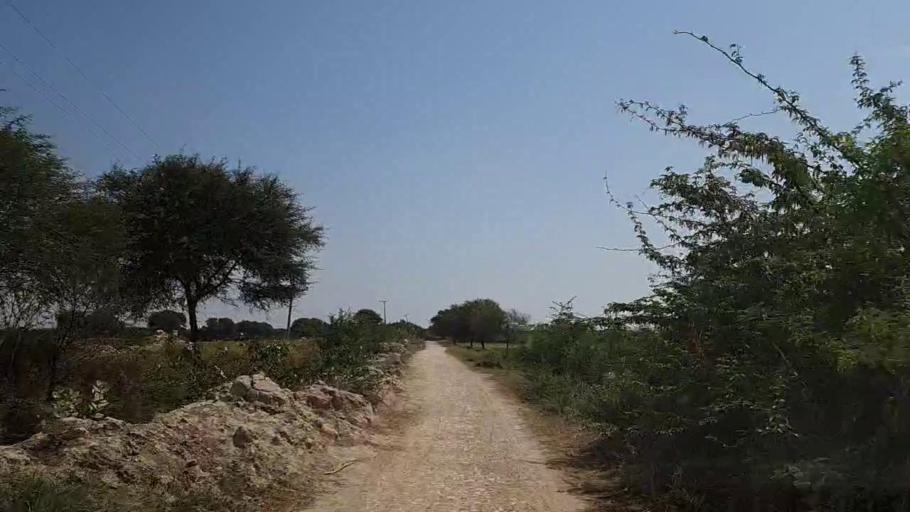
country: PK
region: Sindh
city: Mirpur Batoro
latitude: 24.7751
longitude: 68.2445
